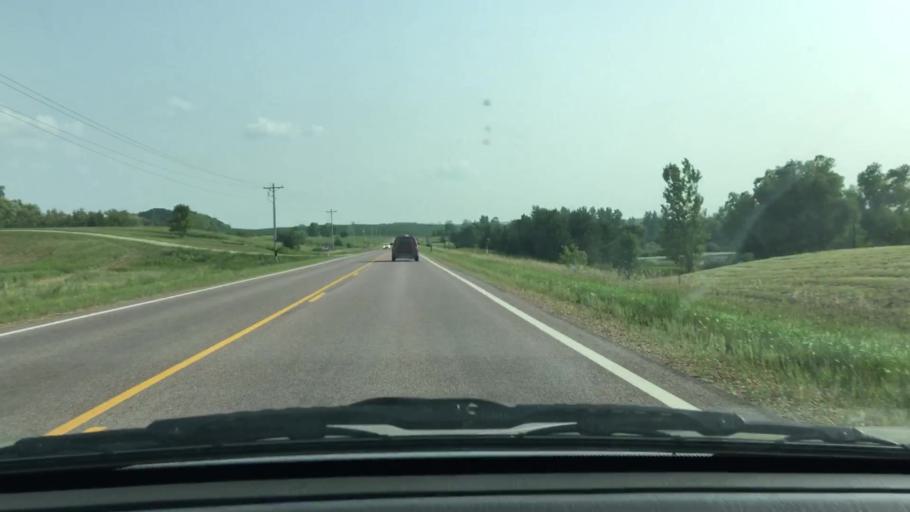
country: US
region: Minnesota
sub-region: Scott County
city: Elko New Market
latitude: 44.5500
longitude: -93.3394
